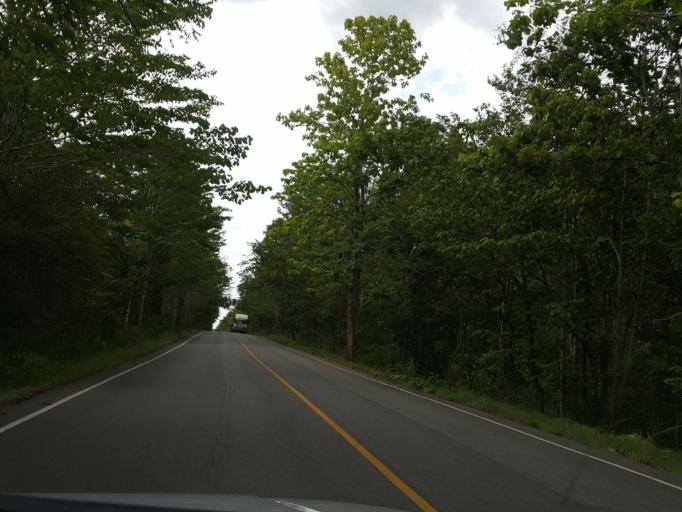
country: TH
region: Sukhothai
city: Thung Saliam
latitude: 17.4022
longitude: 99.3908
